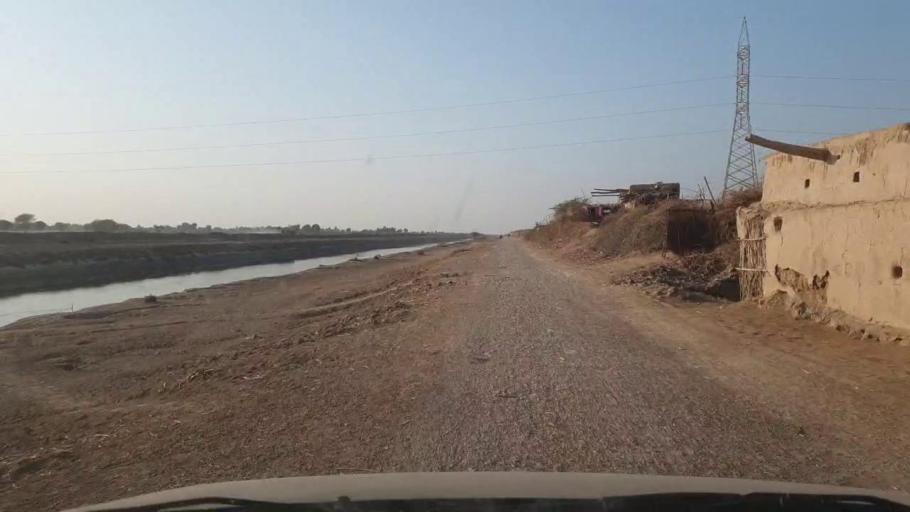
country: PK
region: Sindh
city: Samaro
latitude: 25.2805
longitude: 69.3410
